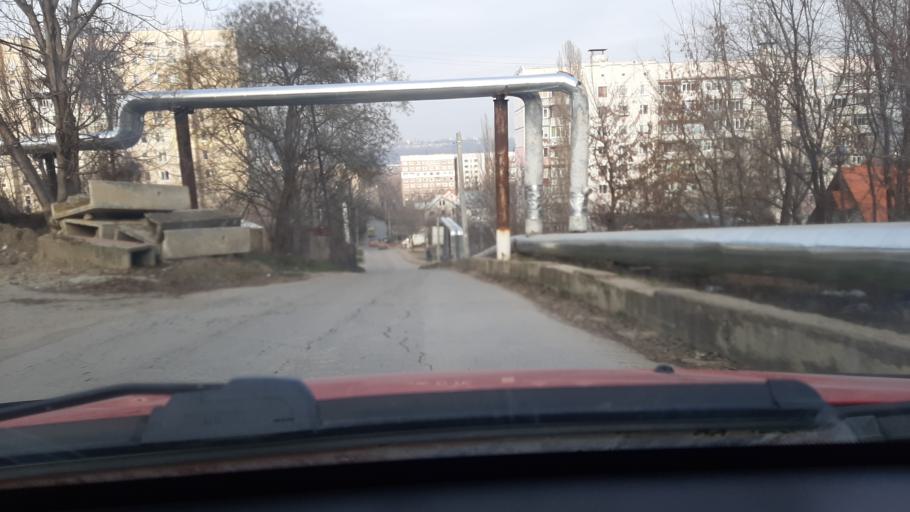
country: MD
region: Chisinau
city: Vatra
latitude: 47.0395
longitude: 28.7893
